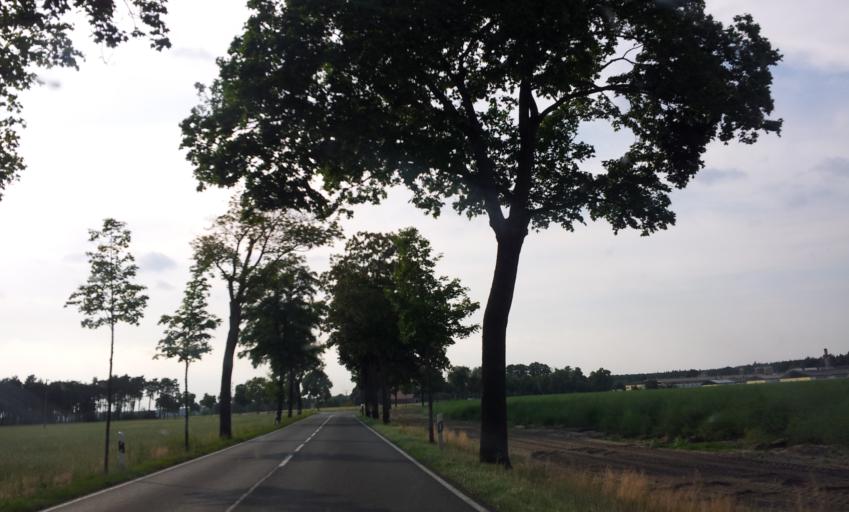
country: DE
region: Brandenburg
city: Beelitz
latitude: 52.1343
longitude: 12.9966
